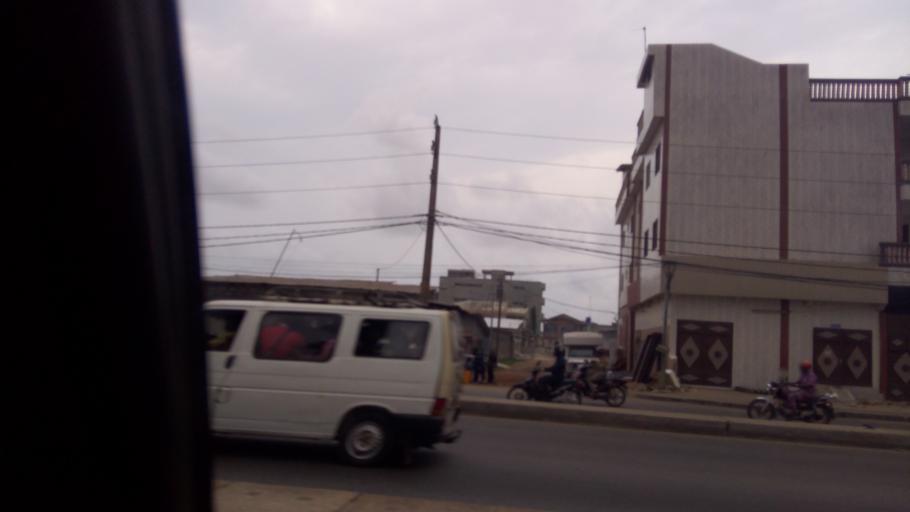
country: BJ
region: Littoral
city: Cotonou
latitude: 6.3773
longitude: 2.3859
